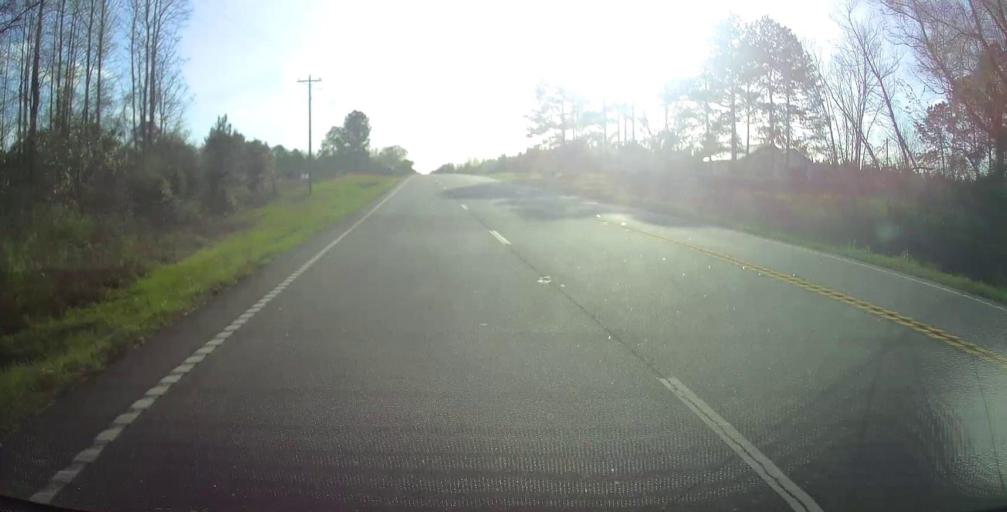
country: US
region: Georgia
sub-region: Tattnall County
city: Reidsville
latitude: 32.1110
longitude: -82.0840
